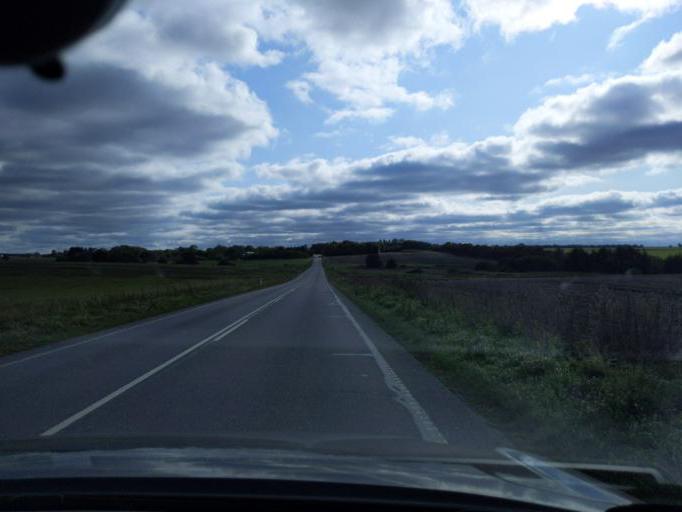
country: DK
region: North Denmark
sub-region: Mariagerfjord Kommune
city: Hobro
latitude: 56.5368
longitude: 9.7258
